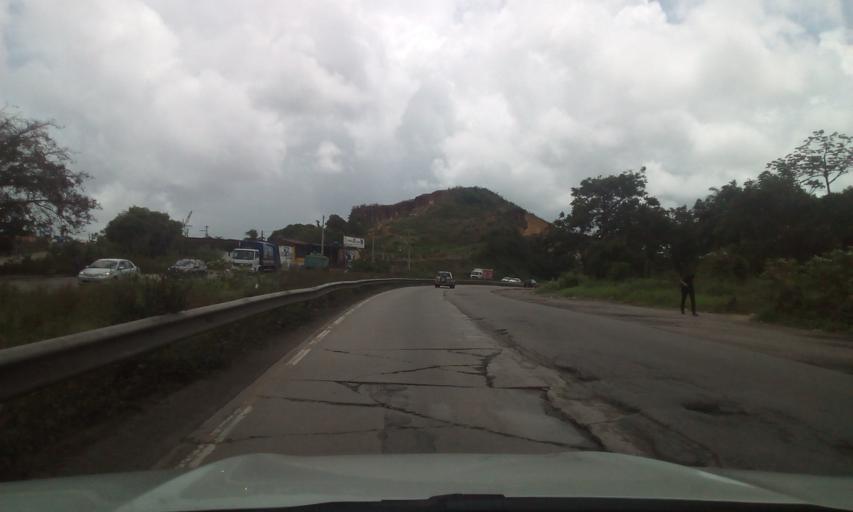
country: BR
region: Pernambuco
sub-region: Jaboatao Dos Guararapes
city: Jaboatao dos Guararapes
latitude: -8.1067
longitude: -34.9483
